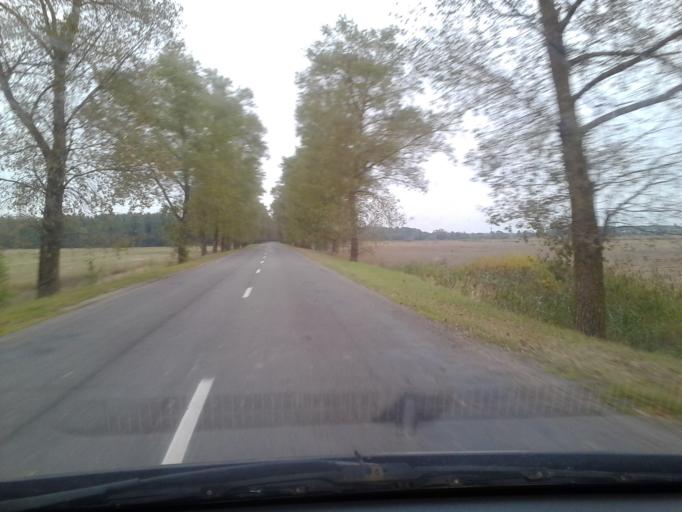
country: BY
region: Vitebsk
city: Pastavy
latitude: 55.1528
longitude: 26.9721
